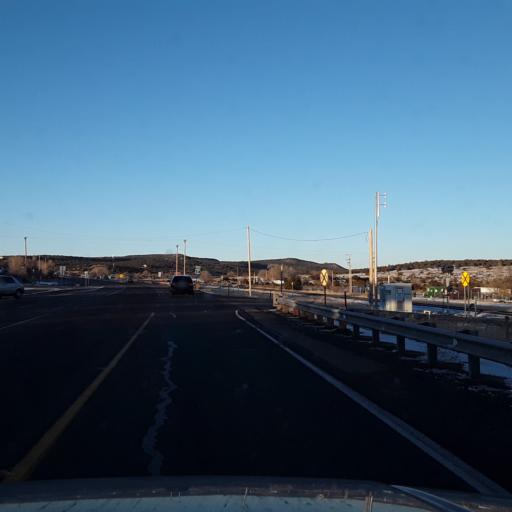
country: US
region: New Mexico
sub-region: Lincoln County
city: Carrizozo
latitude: 34.2442
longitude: -105.5954
